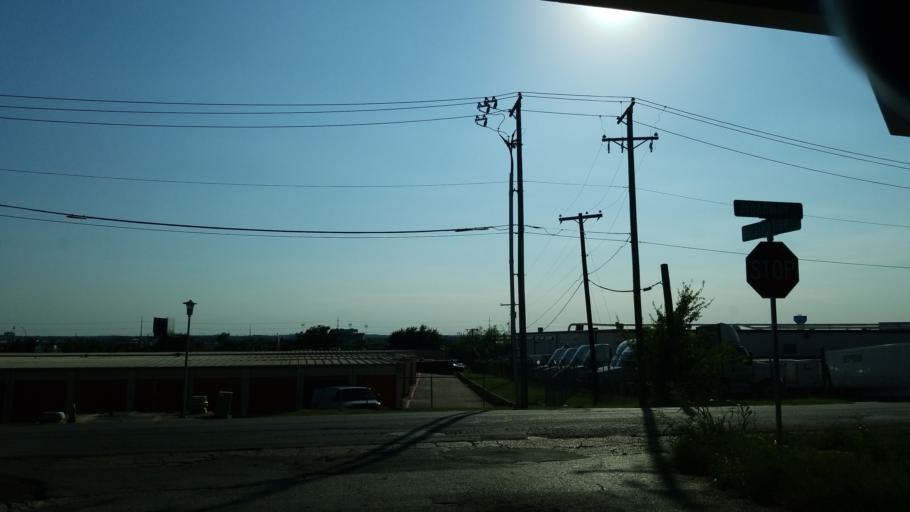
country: US
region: Texas
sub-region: Dallas County
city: Carrollton
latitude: 32.9430
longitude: -96.9005
